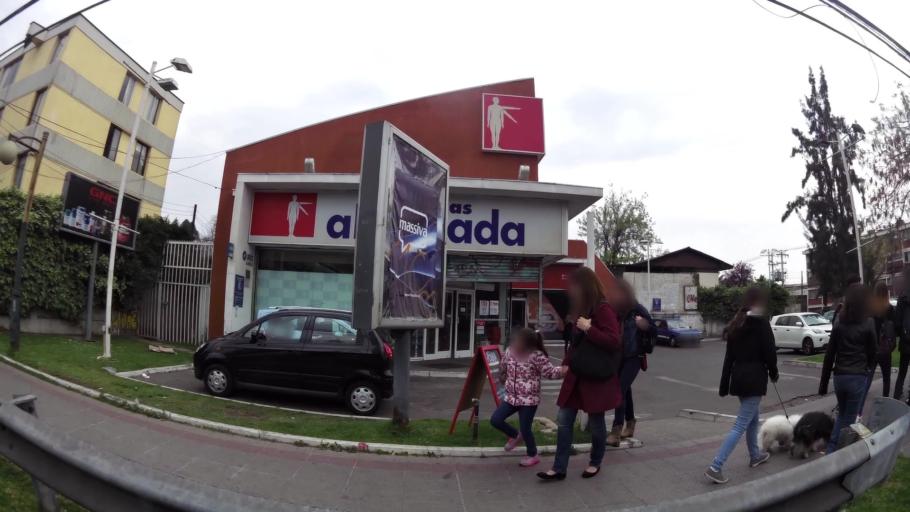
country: CL
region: Santiago Metropolitan
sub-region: Provincia de Santiago
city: Villa Presidente Frei, Nunoa, Santiago, Chile
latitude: -33.4648
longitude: -70.5999
